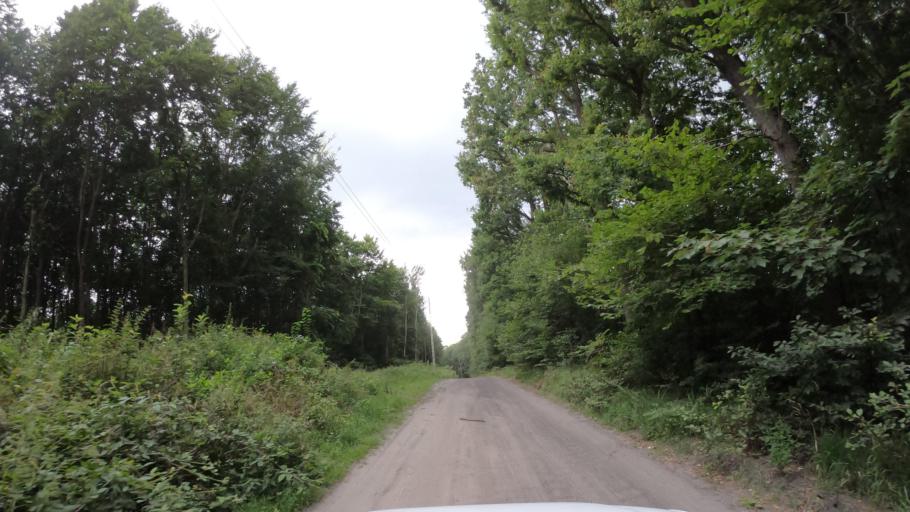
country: PL
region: West Pomeranian Voivodeship
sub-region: Powiat stargardzki
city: Dolice
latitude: 53.1969
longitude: 15.2764
